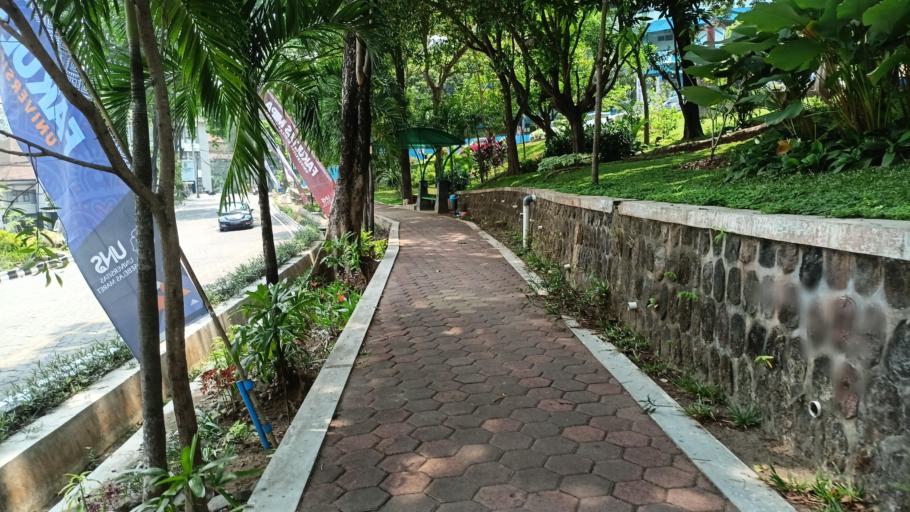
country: ID
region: Central Java
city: Surakarta
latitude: -7.5597
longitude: 110.8579
